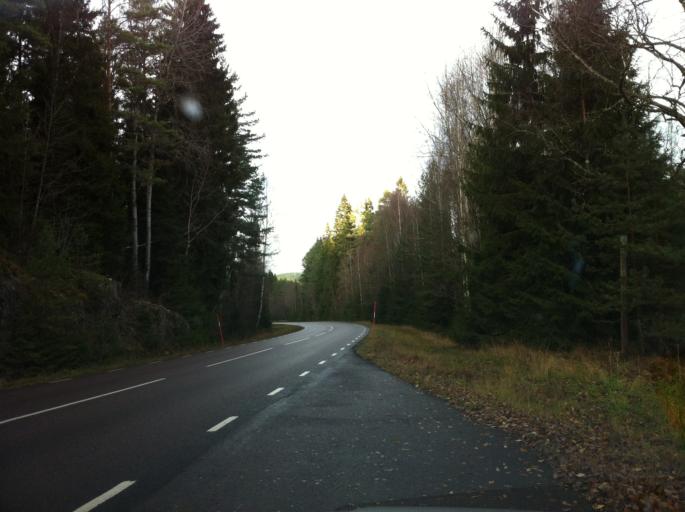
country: SE
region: Kalmar
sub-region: Hultsfreds Kommun
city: Virserum
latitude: 57.2665
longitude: 15.5641
